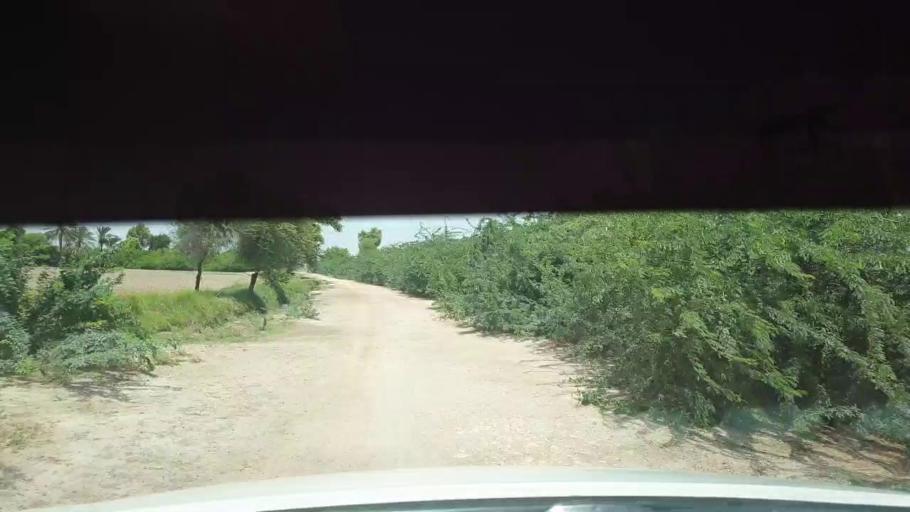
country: PK
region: Sindh
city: Kadhan
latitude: 24.5470
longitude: 68.9695
